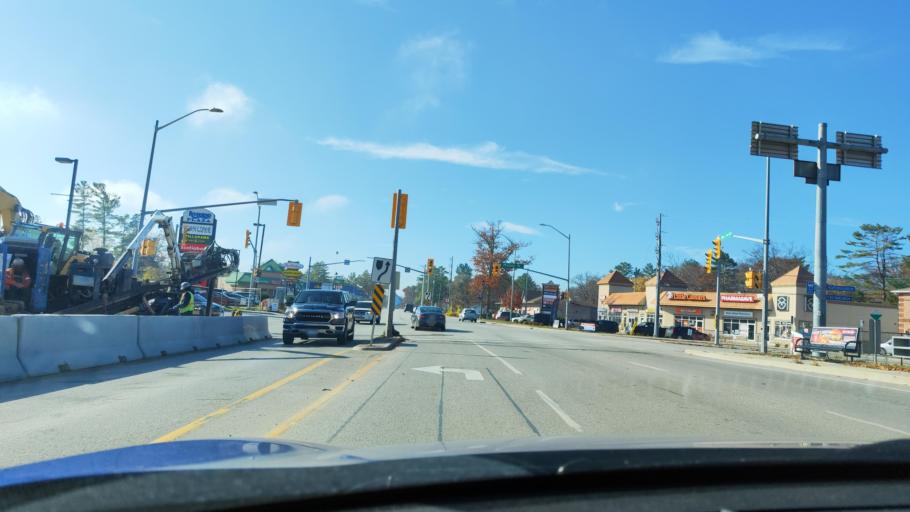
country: CA
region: Ontario
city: Wasaga Beach
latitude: 44.4895
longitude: -80.0508
